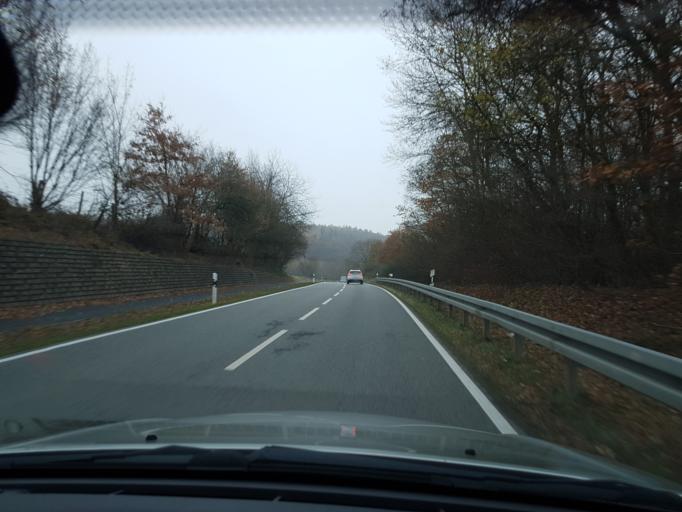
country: DE
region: Hesse
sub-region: Regierungsbezirk Darmstadt
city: Schlangenbad
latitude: 50.1067
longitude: 8.0801
